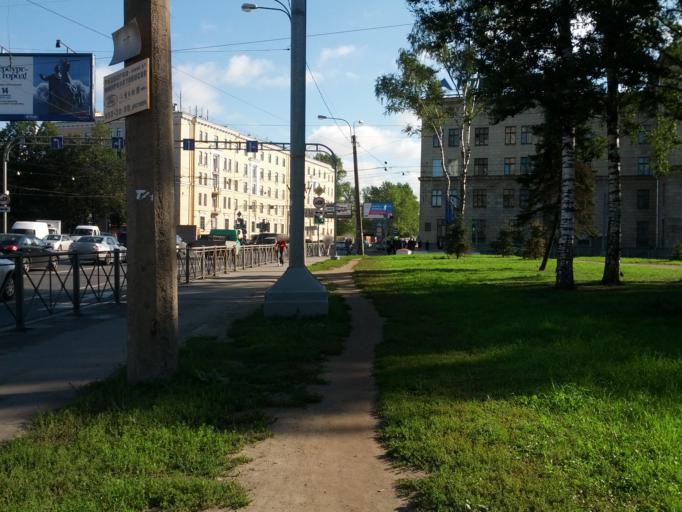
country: RU
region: Leningrad
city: Sampsonievskiy
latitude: 59.9839
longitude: 30.3342
